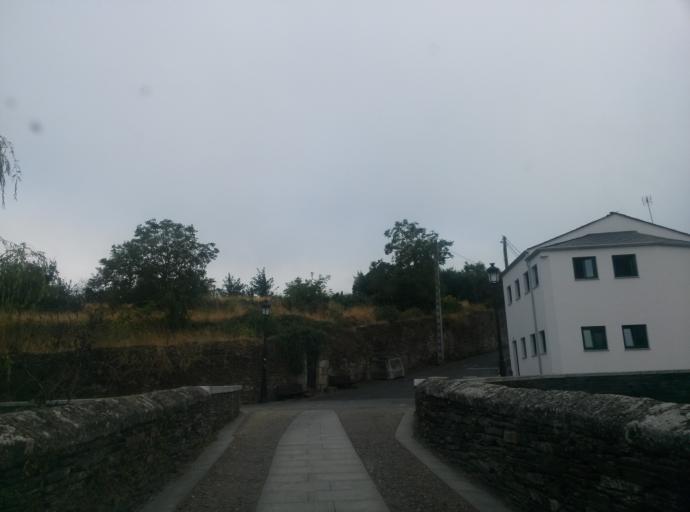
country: ES
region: Galicia
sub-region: Provincia de Lugo
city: Lugo
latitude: 43.0137
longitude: -7.5462
